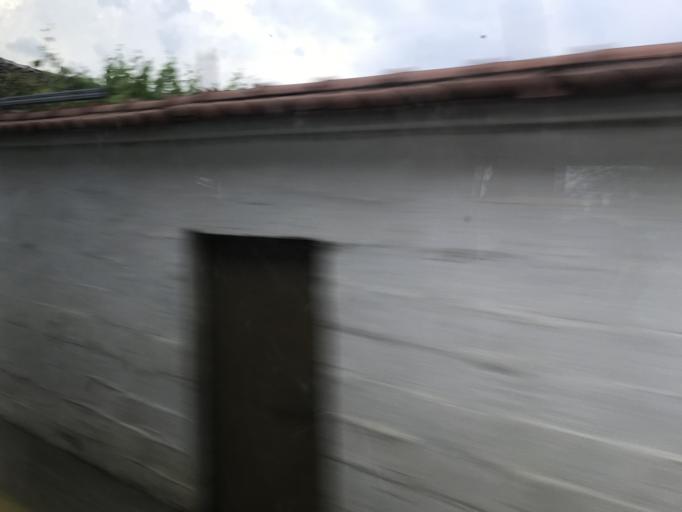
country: GR
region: East Macedonia and Thrace
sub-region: Nomos Rodopis
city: Aratos
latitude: 41.0804
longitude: 25.5557
